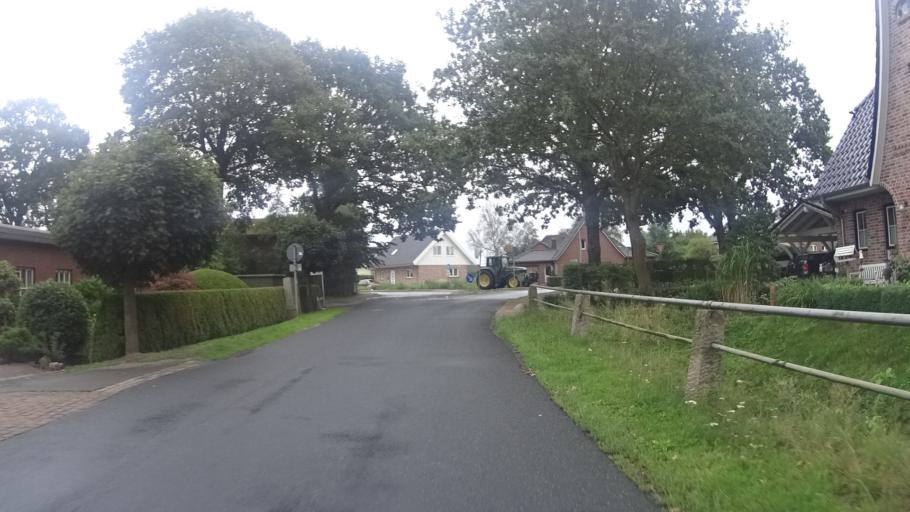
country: DE
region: Schleswig-Holstein
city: Kiebitzreihe
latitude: 53.7837
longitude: 9.6099
